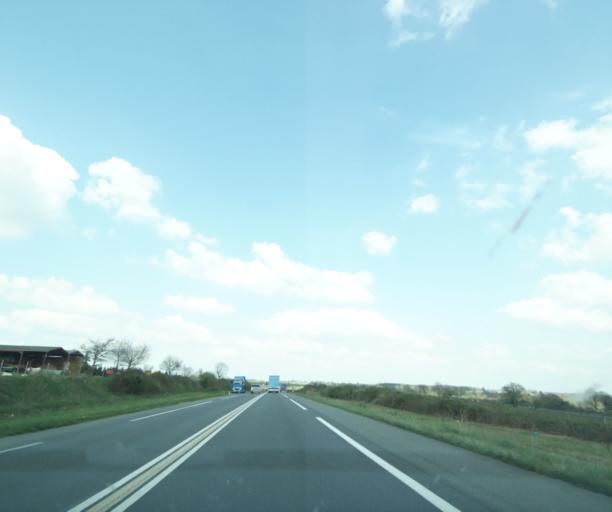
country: FR
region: Auvergne
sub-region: Departement de l'Allier
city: Montmarault
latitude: 46.3337
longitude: 2.9768
